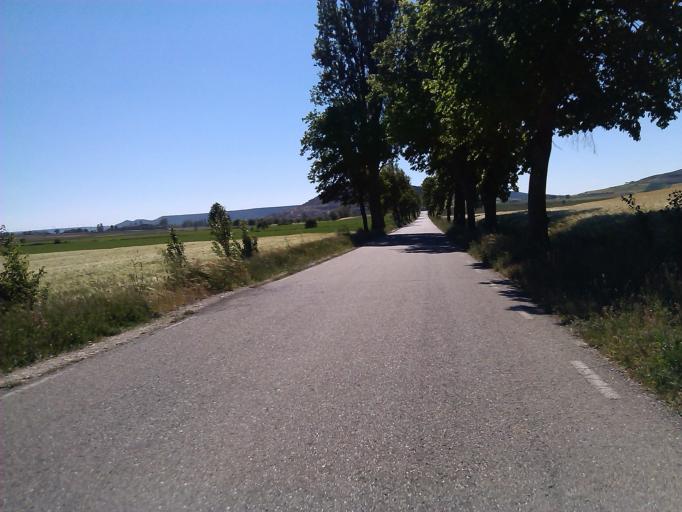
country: ES
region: Castille and Leon
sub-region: Provincia de Burgos
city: Villaquiran de la Puebla
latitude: 42.2918
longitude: -4.1098
